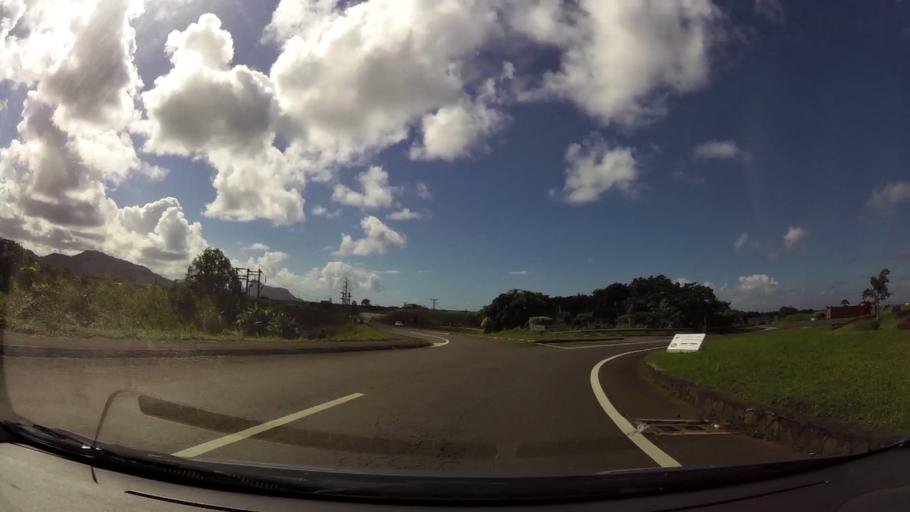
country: MU
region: Grand Port
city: Plaine Magnien
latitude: -20.4201
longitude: 57.6661
